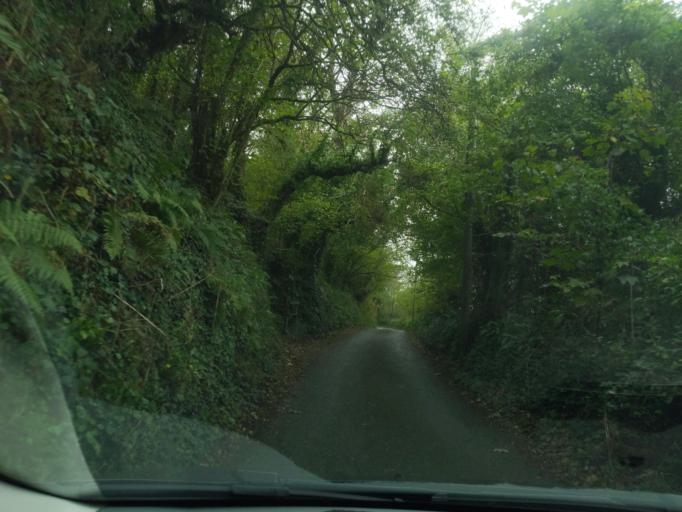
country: GB
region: England
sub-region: Cornwall
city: Looe
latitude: 50.3657
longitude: -4.3947
